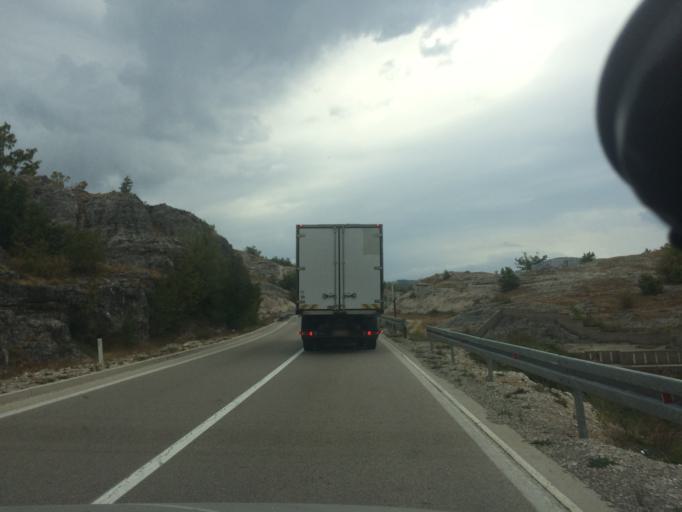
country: ME
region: Kotor
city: Risan
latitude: 42.6975
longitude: 18.6289
